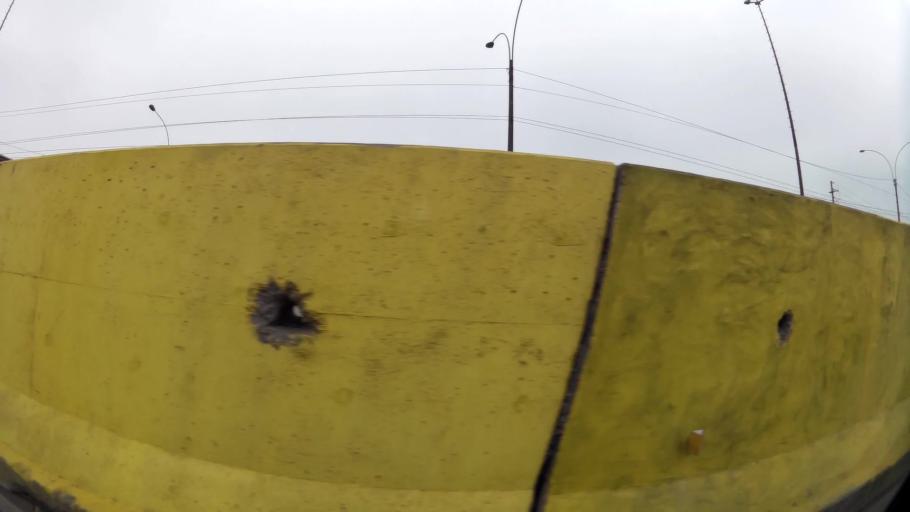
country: PE
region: Lima
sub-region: Lima
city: Urb. Santo Domingo
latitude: -11.9080
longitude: -77.0703
